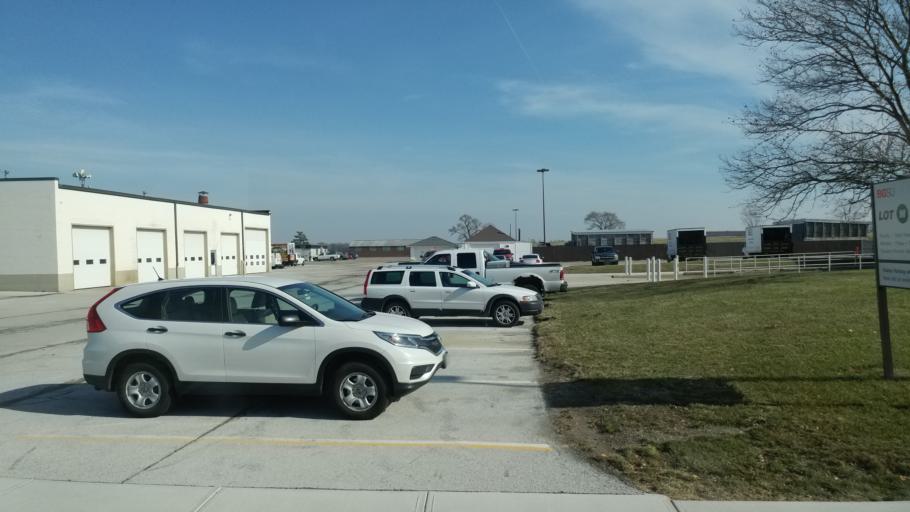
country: US
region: Ohio
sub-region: Wood County
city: Bowling Green
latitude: 41.3838
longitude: -83.6396
